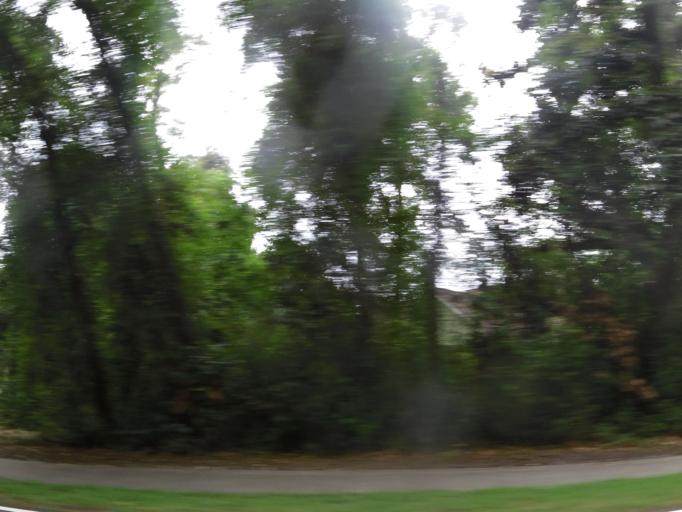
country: US
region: Georgia
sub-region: Glynn County
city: Saint Simon Mills
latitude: 31.1634
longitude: -81.3993
